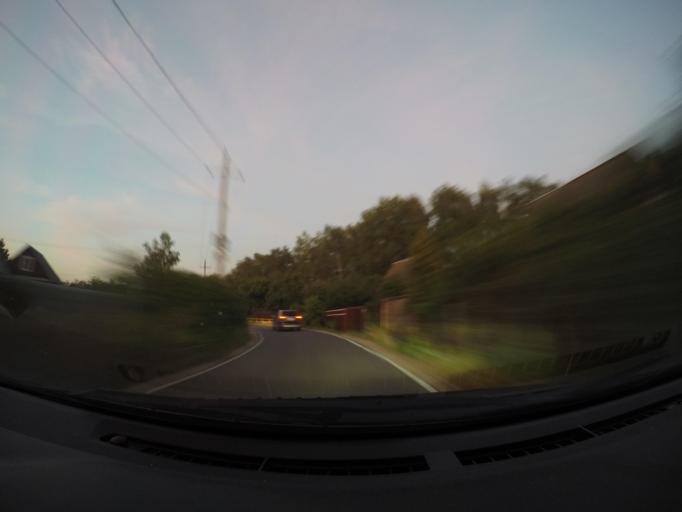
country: RU
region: Moskovskaya
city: Rechitsy
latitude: 55.5471
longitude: 38.4562
